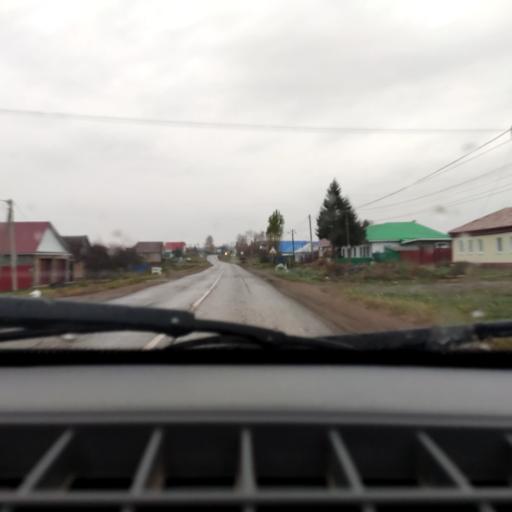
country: RU
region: Bashkortostan
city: Avdon
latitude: 54.6544
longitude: 55.7760
